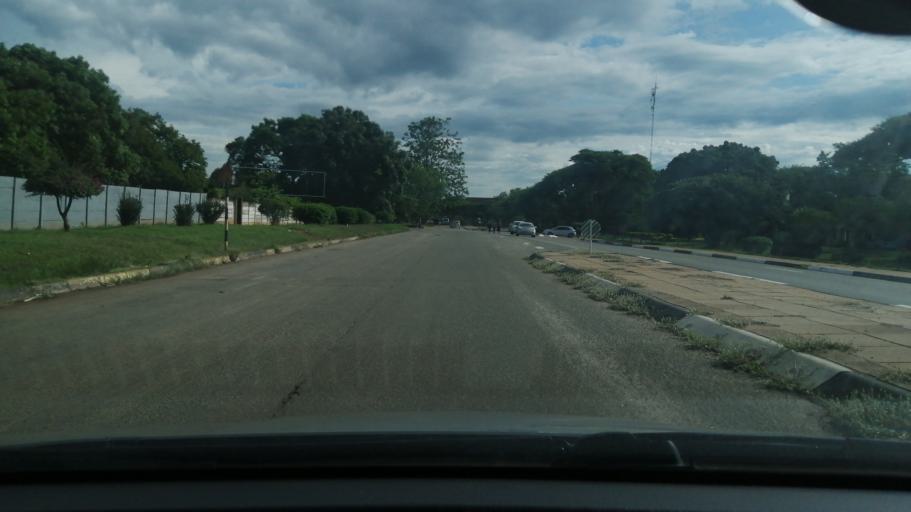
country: ZW
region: Harare
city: Harare
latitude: -17.7645
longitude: 30.9797
